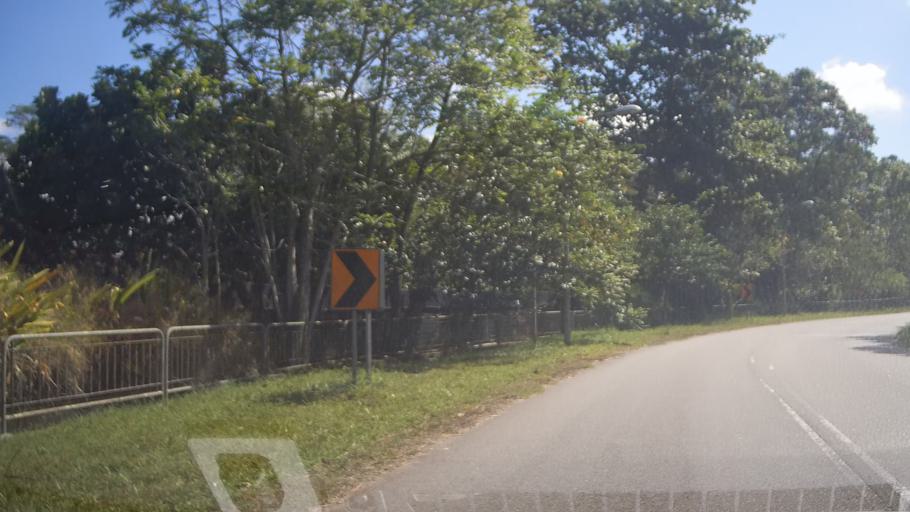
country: MY
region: Johor
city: Johor Bahru
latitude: 1.4358
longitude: 103.7183
